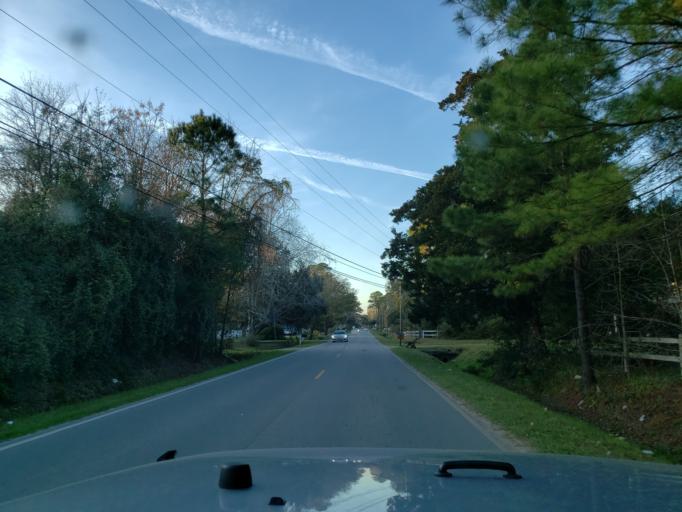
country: US
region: Georgia
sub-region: Chatham County
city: Georgetown
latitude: 32.0245
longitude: -81.2158
